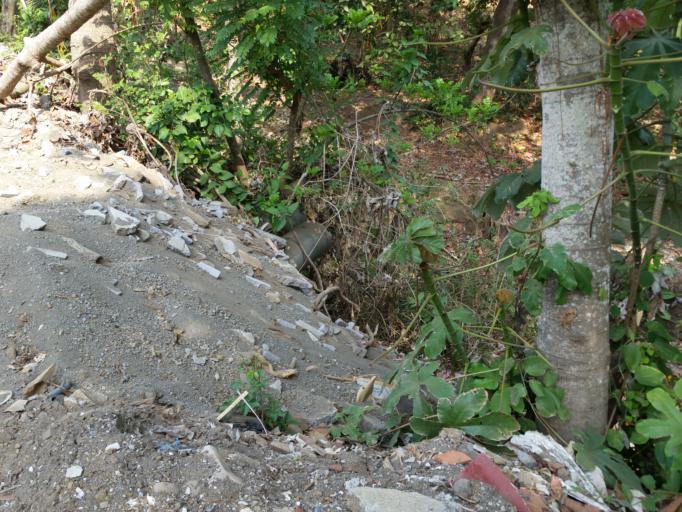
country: NI
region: Masaya
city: Ticuantepe
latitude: 12.0621
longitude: -86.2496
